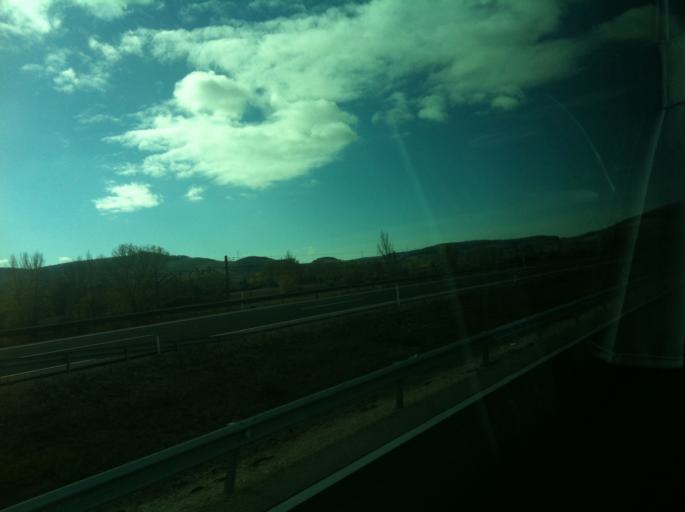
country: ES
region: Castille and Leon
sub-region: Provincia de Burgos
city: Quintanavides
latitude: 42.4807
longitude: -3.4214
